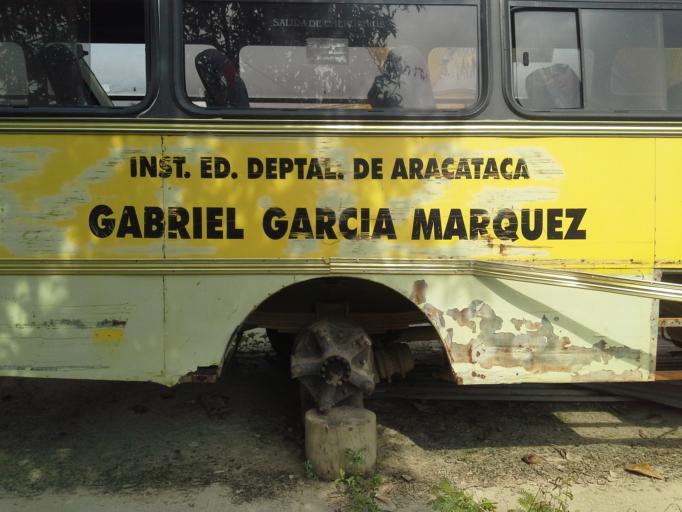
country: CO
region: Magdalena
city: Aracataca
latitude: 10.5861
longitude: -74.1894
